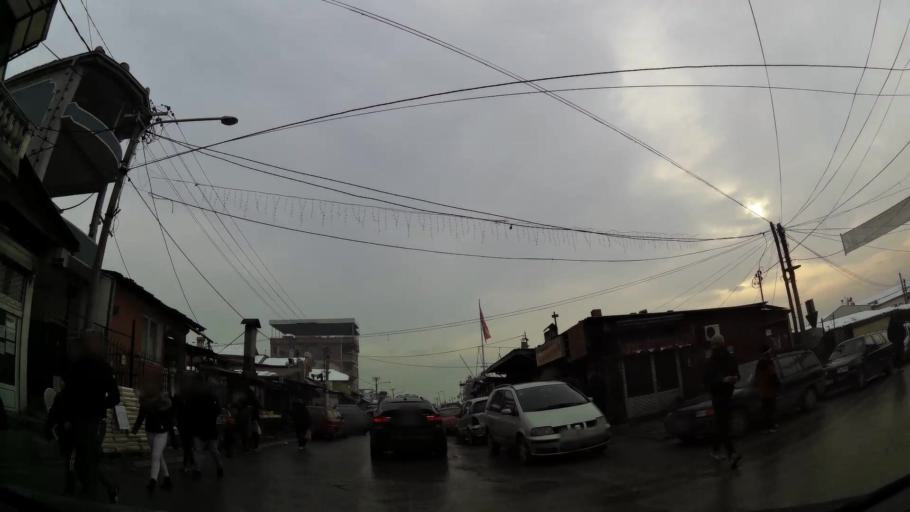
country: MK
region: Suto Orizari
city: Suto Orizare
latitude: 42.0427
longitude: 21.4236
